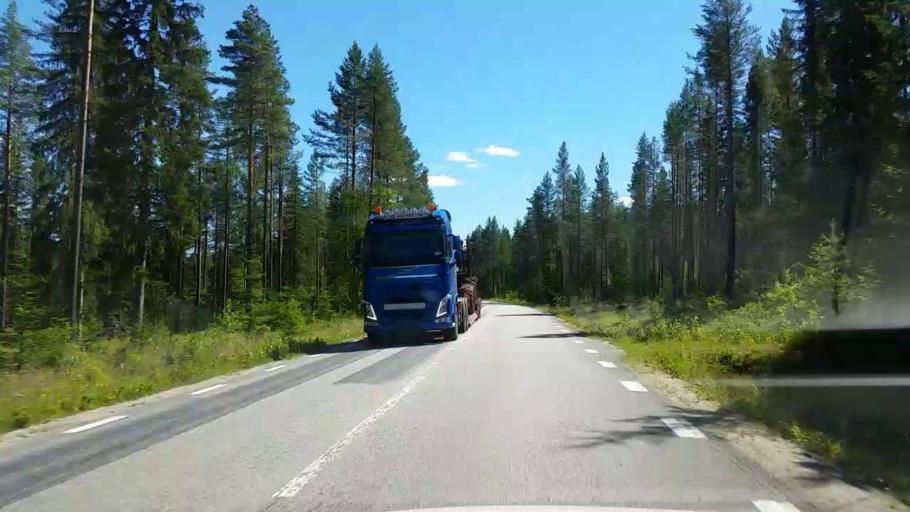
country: SE
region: Gaevleborg
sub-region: Ovanakers Kommun
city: Edsbyn
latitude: 61.3415
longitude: 15.8215
